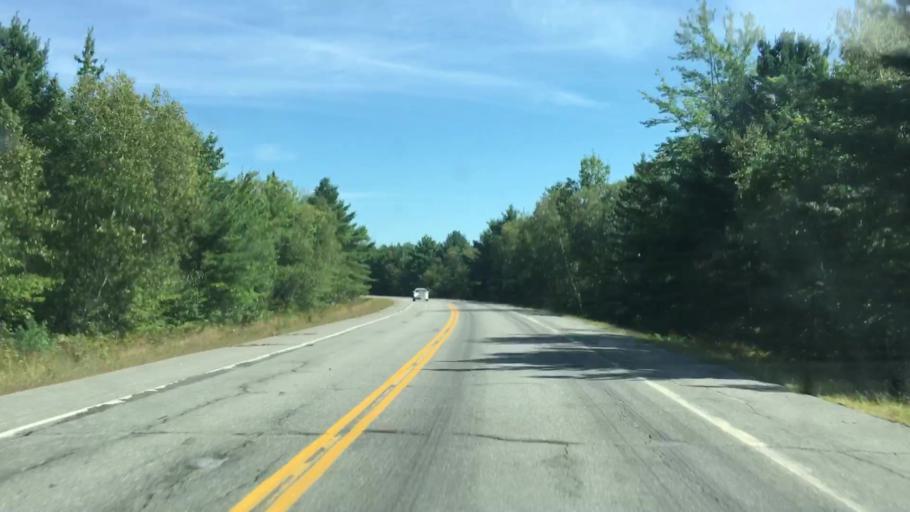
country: US
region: Maine
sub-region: Piscataquis County
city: Milo
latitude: 45.2296
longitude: -68.9513
